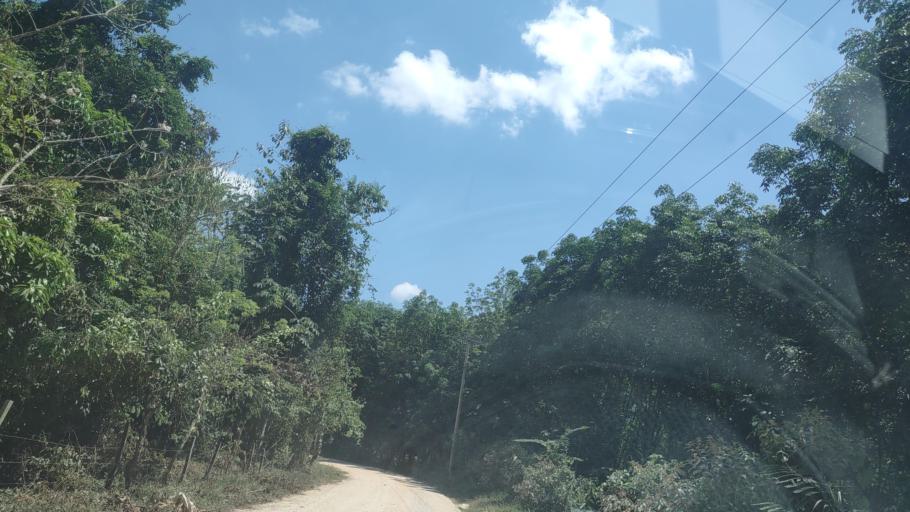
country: MX
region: Veracruz
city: Las Choapas
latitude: 17.7804
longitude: -94.1407
